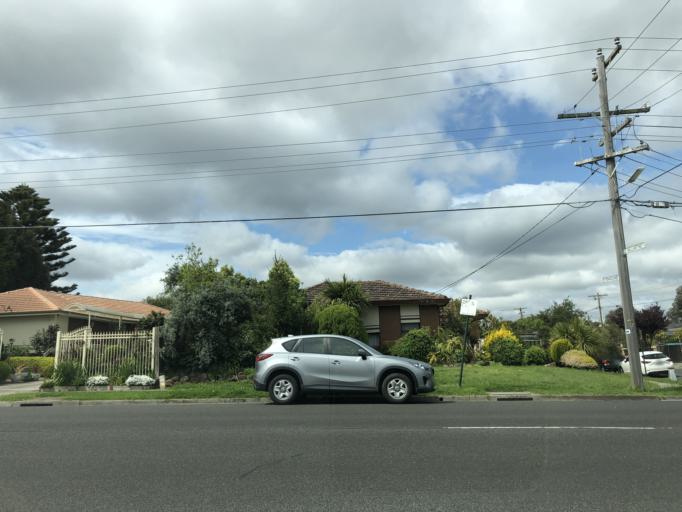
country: AU
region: Victoria
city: Burwood East
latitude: -37.8505
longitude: 145.1633
